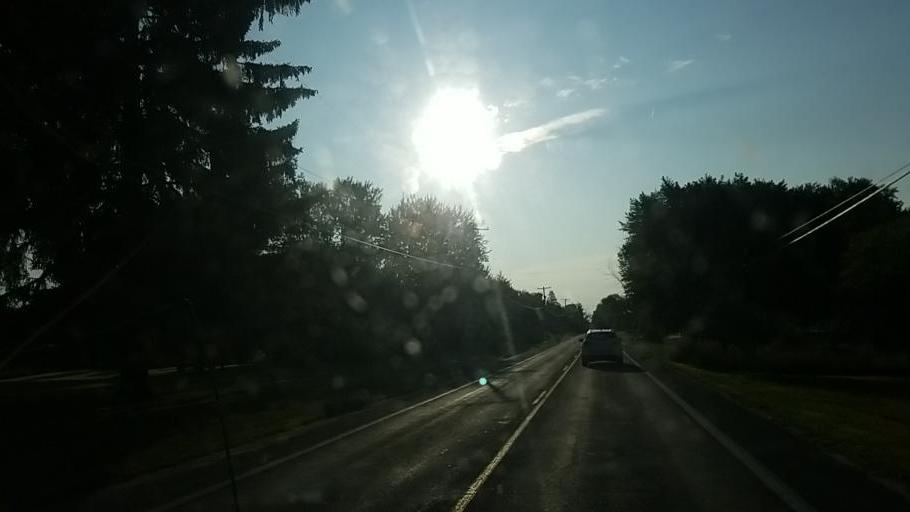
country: US
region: Michigan
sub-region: Montcalm County
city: Stanton
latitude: 43.2499
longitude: -85.1310
